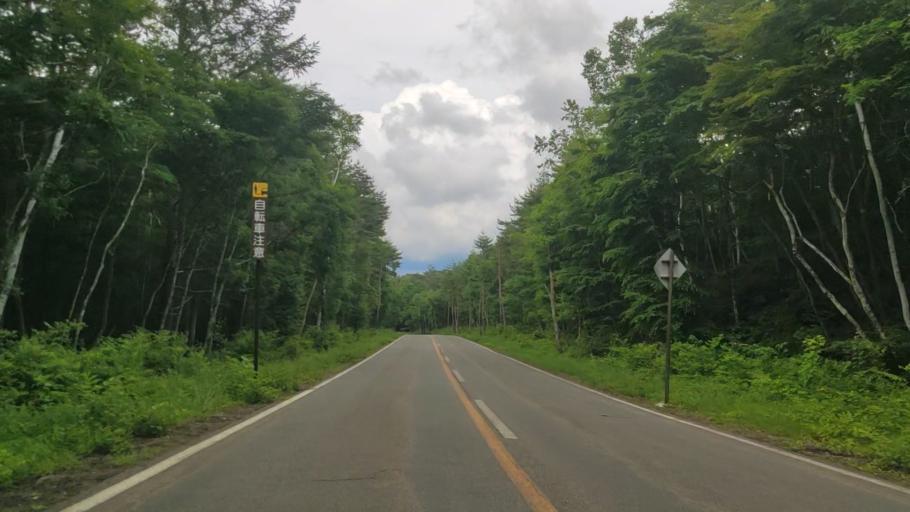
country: JP
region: Yamanashi
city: Fujikawaguchiko
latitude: 35.4347
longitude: 138.7390
